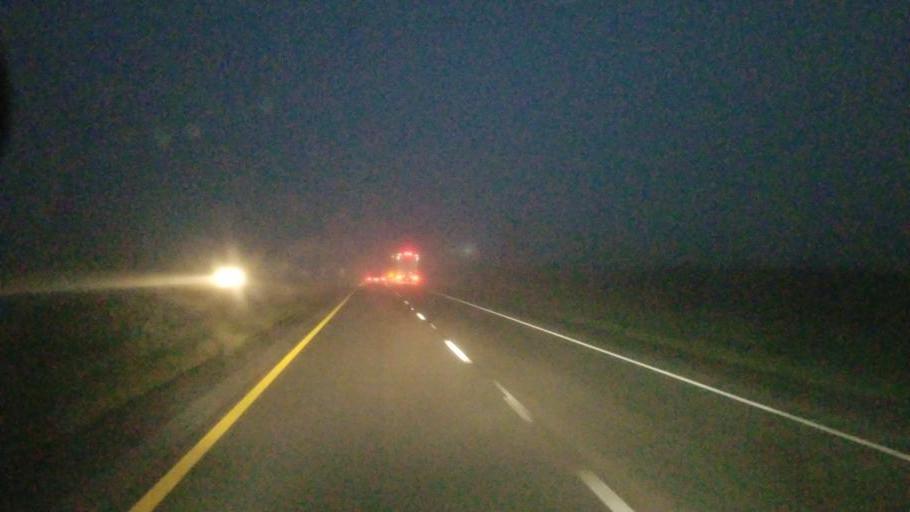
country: US
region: Ohio
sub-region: Ross County
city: Chillicothe
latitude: 39.3572
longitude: -82.9659
